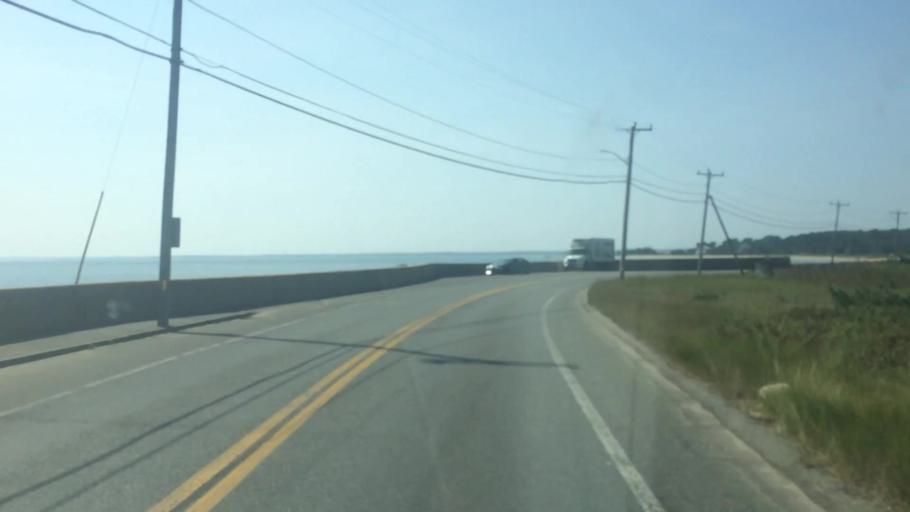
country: US
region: Massachusetts
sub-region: Dukes County
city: Oak Bluffs
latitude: 41.4494
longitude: -70.5529
